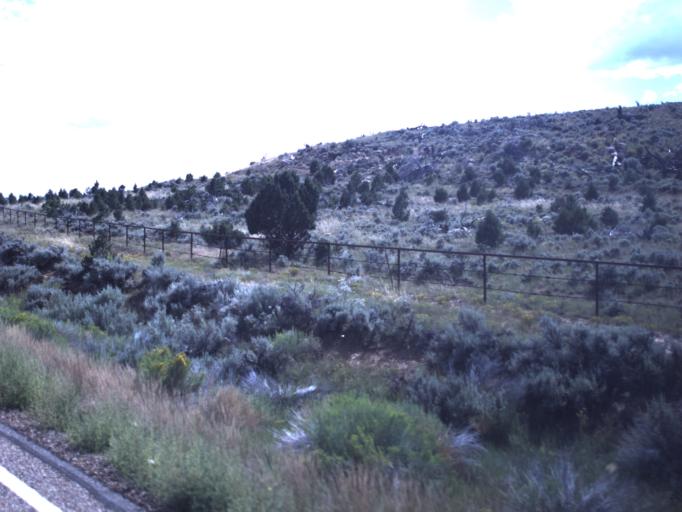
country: US
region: Utah
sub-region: Duchesne County
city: Duchesne
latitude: 40.2912
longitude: -110.6951
